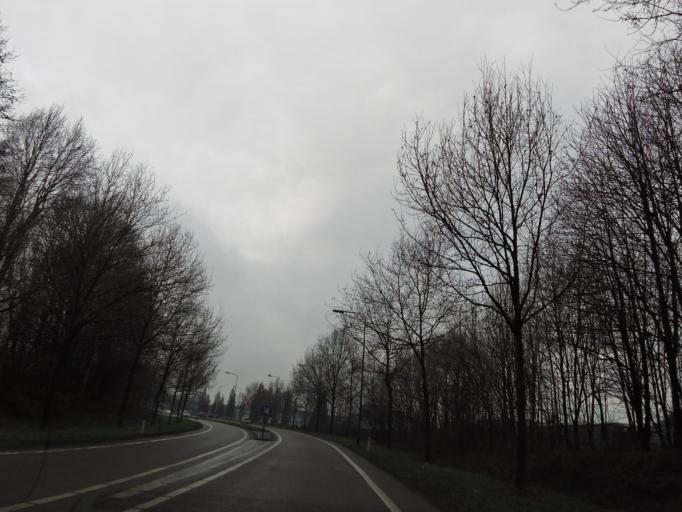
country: NL
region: Limburg
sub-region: Gemeente Simpelveld
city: Simpelveld
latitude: 50.8498
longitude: 6.0129
